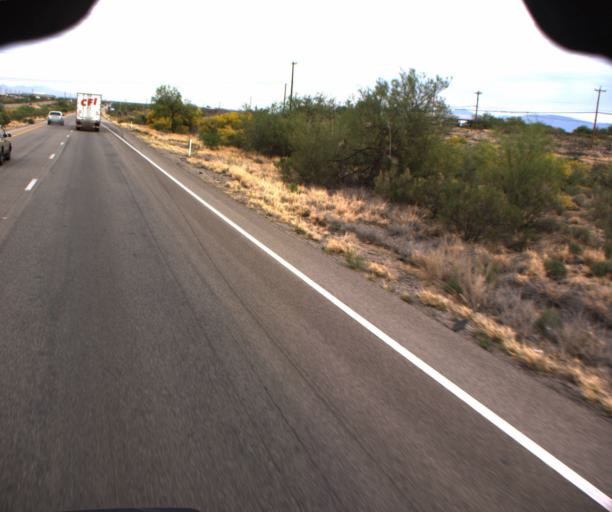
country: US
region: Arizona
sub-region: Pima County
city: Vail
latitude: 32.0122
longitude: -110.6978
